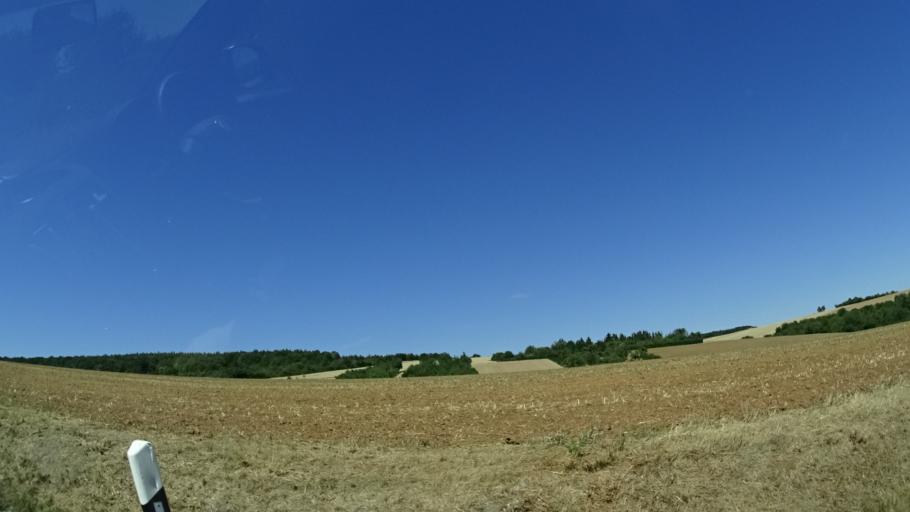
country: DE
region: Bavaria
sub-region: Regierungsbezirk Unterfranken
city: Rimpar
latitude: 49.8619
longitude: 9.9401
